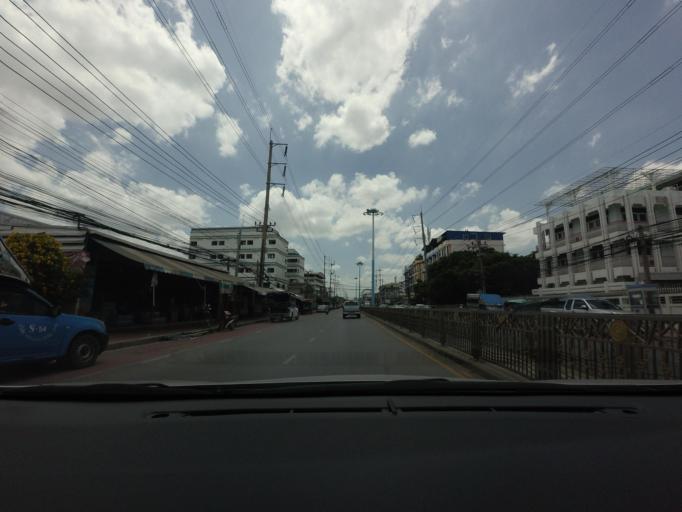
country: TH
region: Samut Prakan
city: Samut Prakan
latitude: 13.5736
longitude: 100.5918
